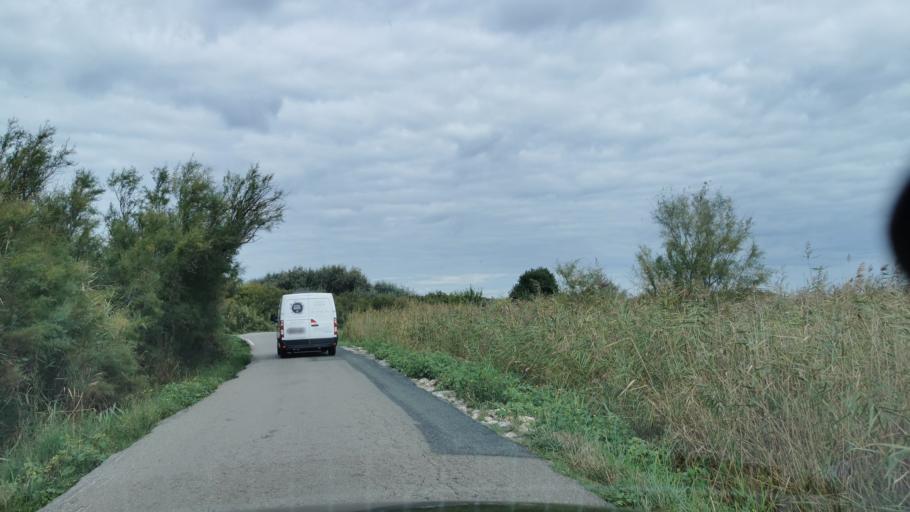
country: FR
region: Languedoc-Roussillon
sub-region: Departement de l'Aude
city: Fleury
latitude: 43.2135
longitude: 3.1945
